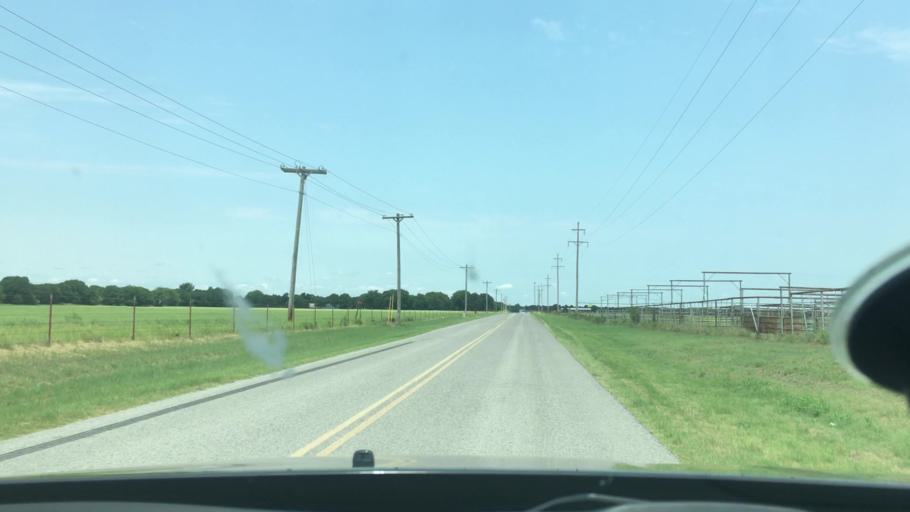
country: US
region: Oklahoma
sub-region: Love County
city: Marietta
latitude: 33.9166
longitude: -97.3521
